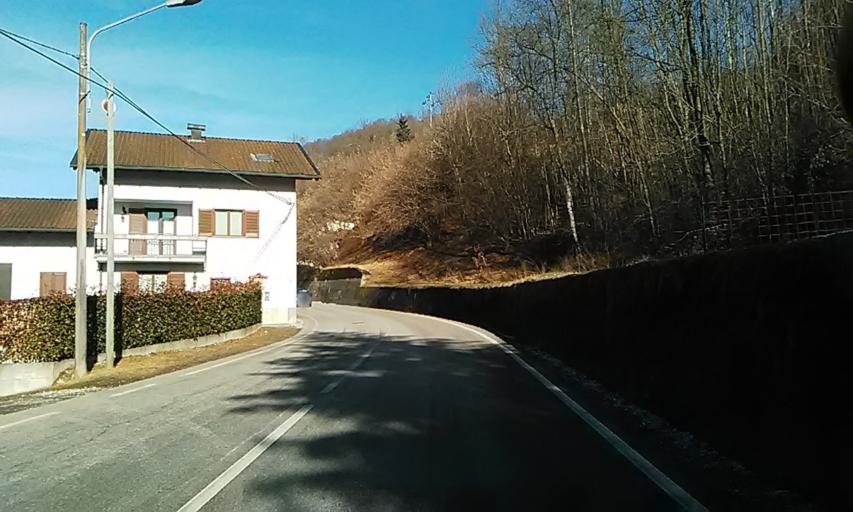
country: IT
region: Piedmont
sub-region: Provincia di Vercelli
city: Cellio
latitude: 45.7321
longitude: 8.2998
